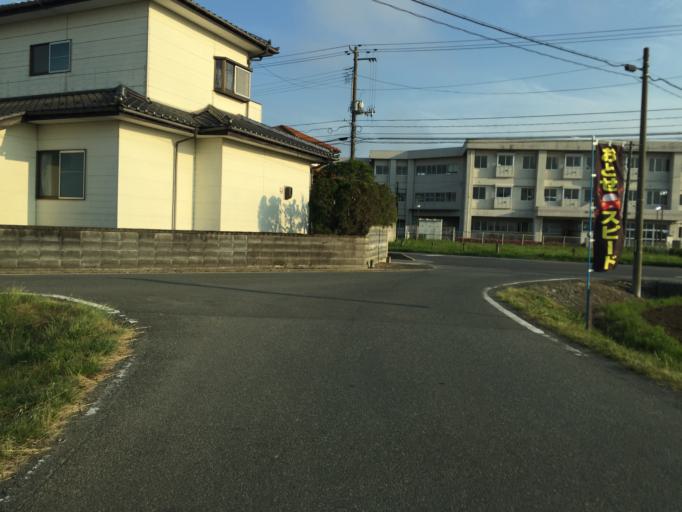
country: JP
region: Miyagi
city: Marumori
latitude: 37.7897
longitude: 140.9492
